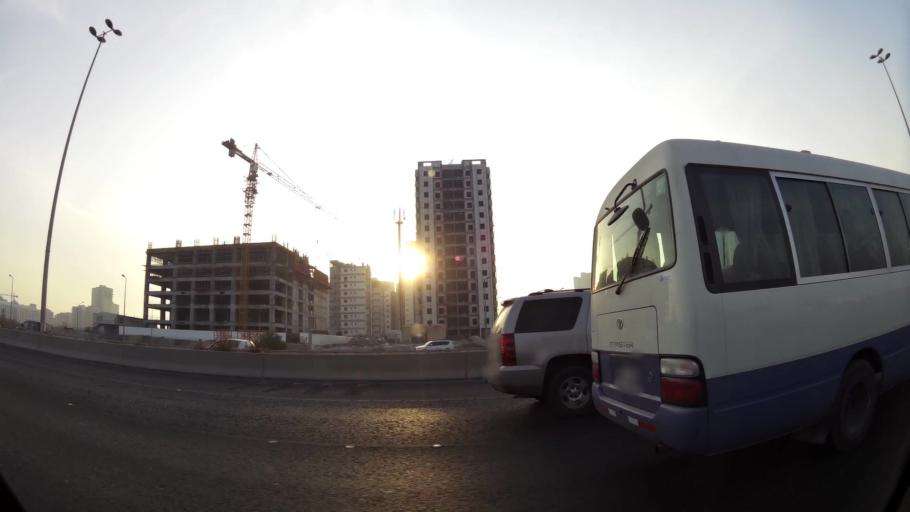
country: KW
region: Mubarak al Kabir
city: Sabah as Salim
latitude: 29.2572
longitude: 48.0890
